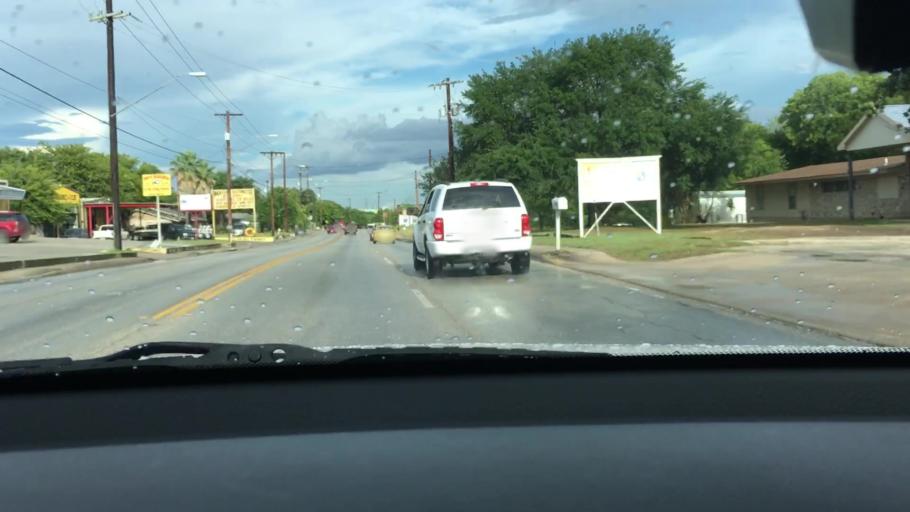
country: US
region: Texas
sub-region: Bexar County
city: Windcrest
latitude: 29.5119
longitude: -98.3635
